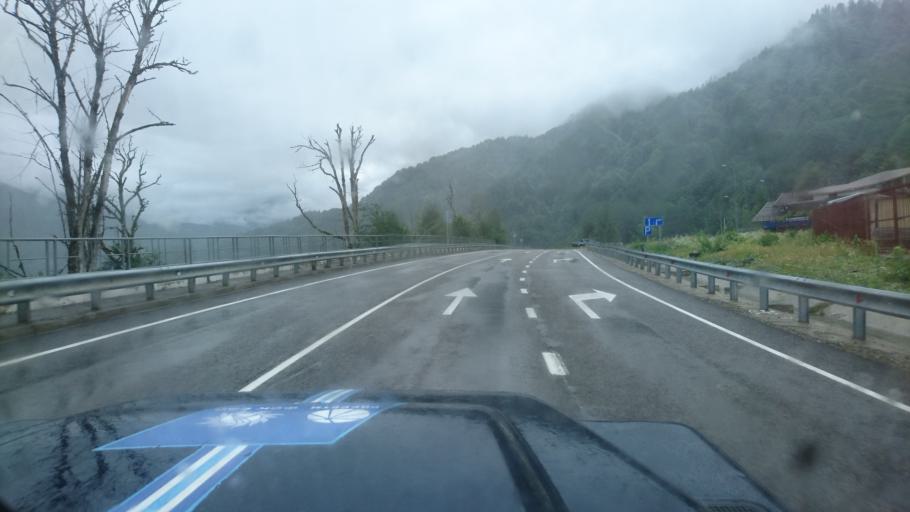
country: RU
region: Krasnodarskiy
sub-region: Sochi City
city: Krasnaya Polyana
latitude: 43.6478
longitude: 40.3399
